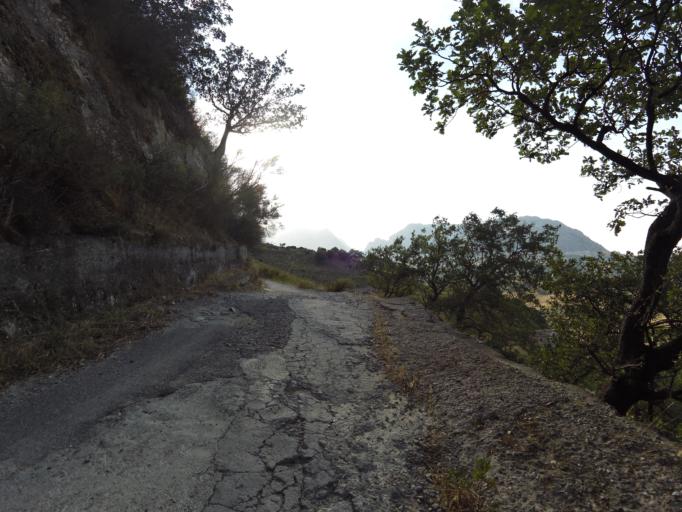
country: IT
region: Calabria
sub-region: Provincia di Reggio Calabria
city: Stilo
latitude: 38.4657
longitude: 16.4848
